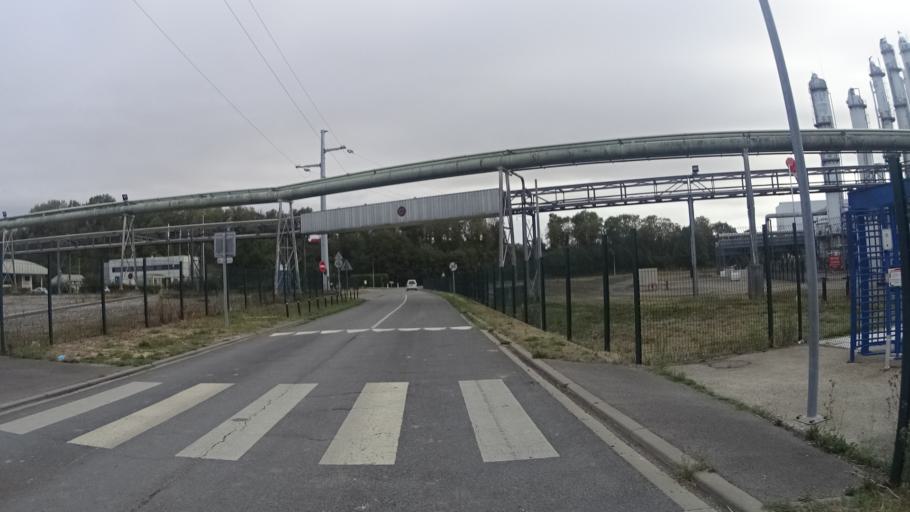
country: FR
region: Picardie
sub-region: Departement de l'Aisne
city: Origny-Sainte-Benoite
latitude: 49.8374
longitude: 3.4752
